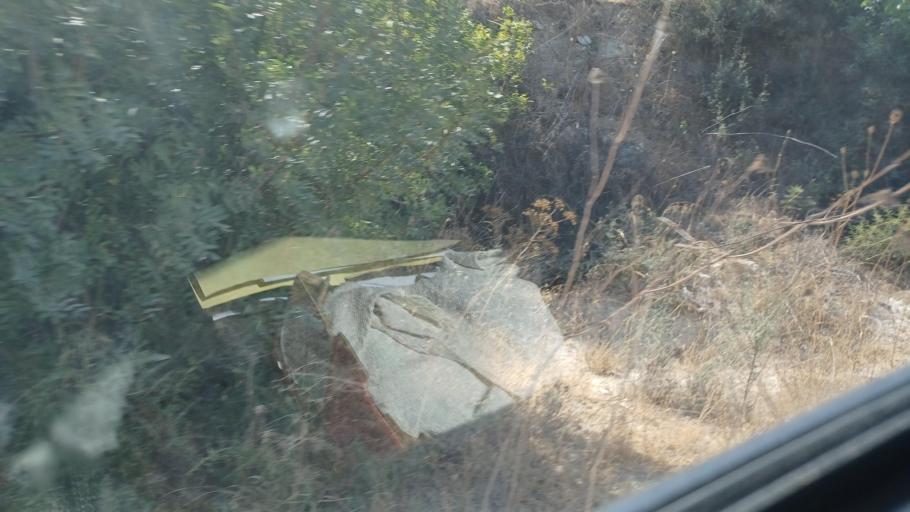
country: CY
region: Pafos
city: Mesogi
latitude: 34.8815
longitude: 32.5322
